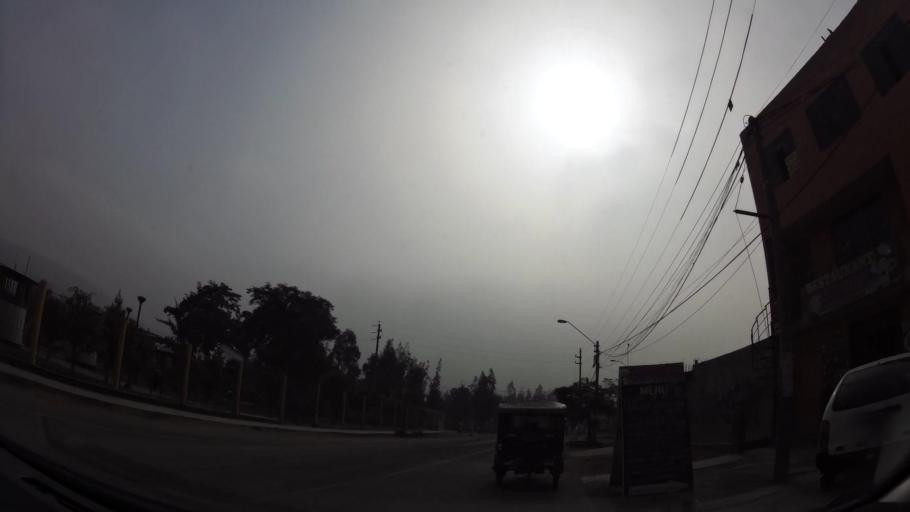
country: PE
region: Lima
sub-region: Lima
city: Santa Maria
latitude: -12.0087
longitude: -76.8333
